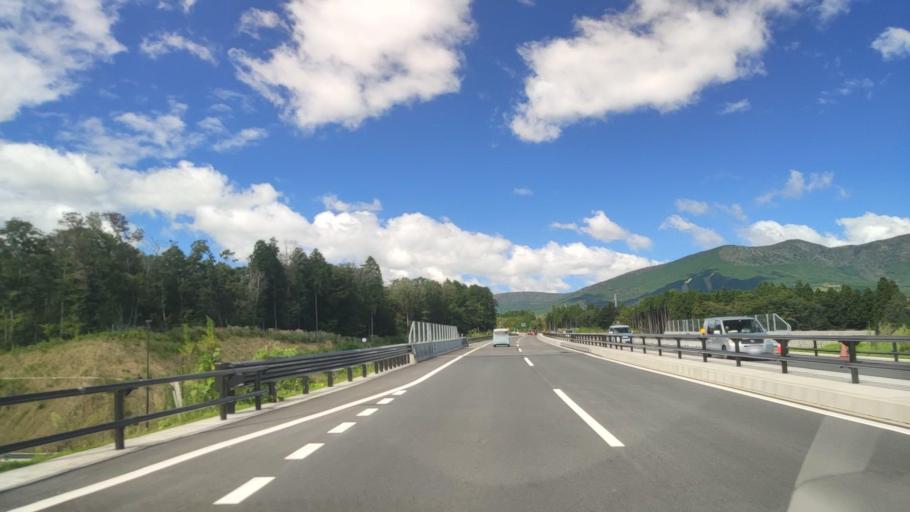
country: JP
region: Shizuoka
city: Gotemba
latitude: 35.3366
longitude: 138.8915
